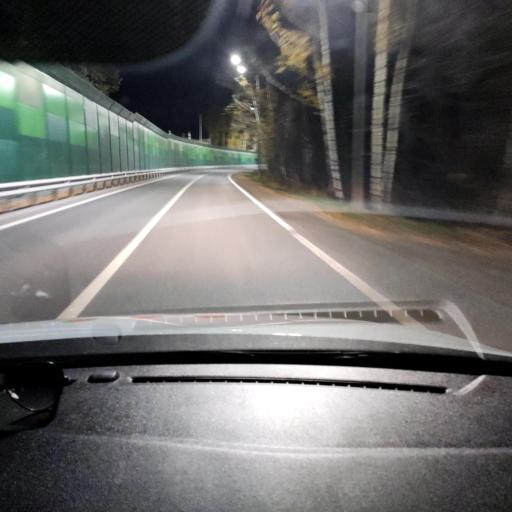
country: RU
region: Tatarstan
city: Verkhniy Uslon
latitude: 55.6277
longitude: 49.0140
